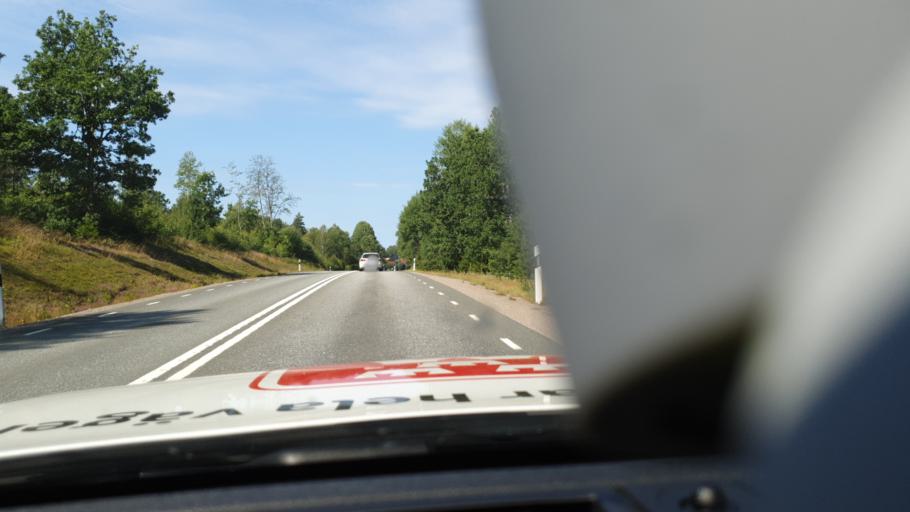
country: SE
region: Kronoberg
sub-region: Uppvidinge Kommun
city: Aseda
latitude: 57.4007
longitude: 15.3314
